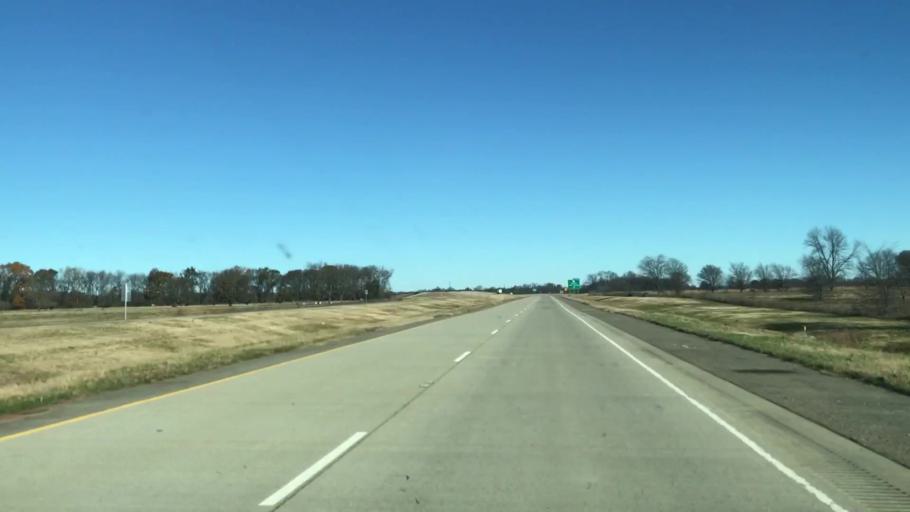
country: US
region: Louisiana
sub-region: Caddo Parish
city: Vivian
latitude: 32.8861
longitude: -93.8598
